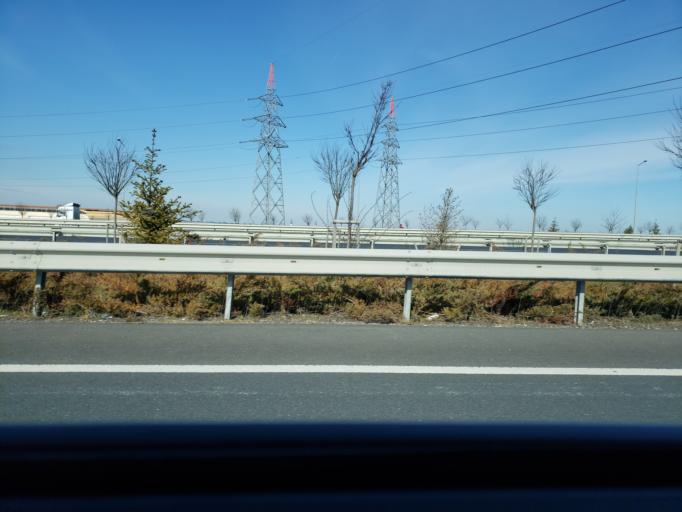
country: TR
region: Istanbul
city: Durusu
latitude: 41.2452
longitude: 28.7447
